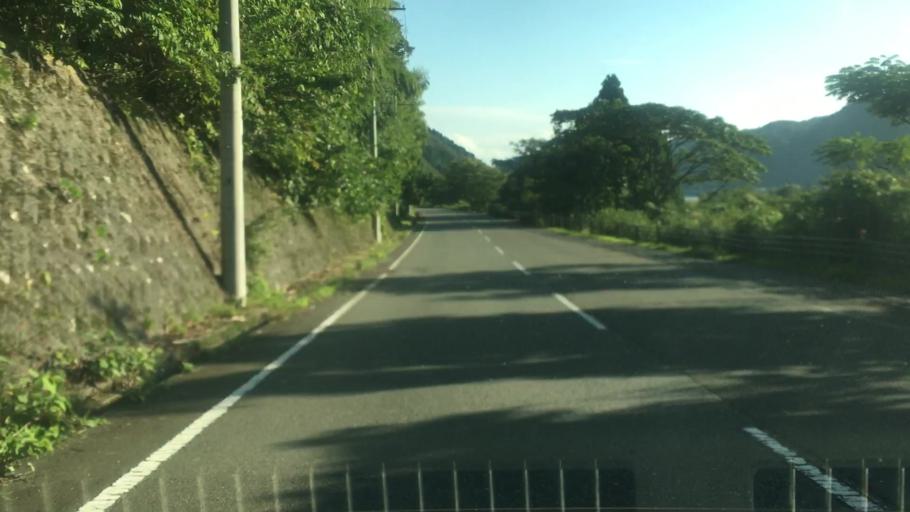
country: JP
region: Hyogo
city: Toyooka
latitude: 35.6037
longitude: 134.8060
